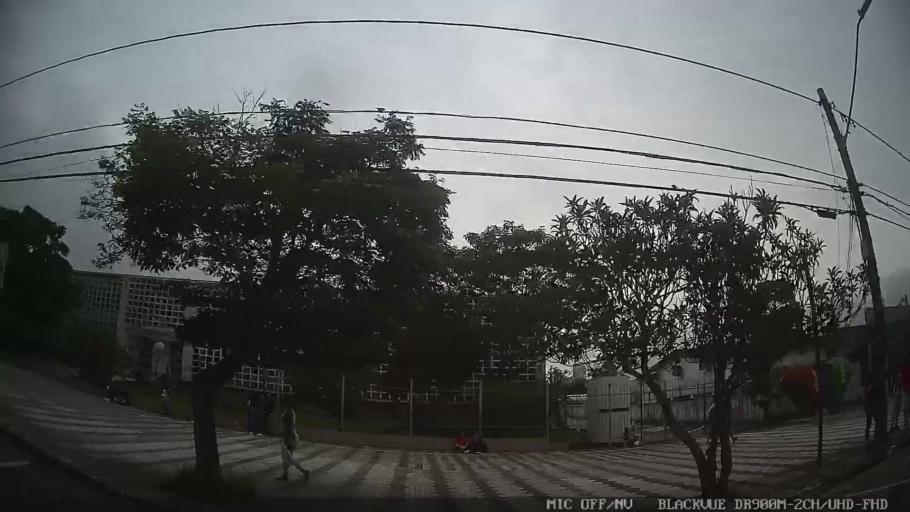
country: BR
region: Sao Paulo
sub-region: Mogi das Cruzes
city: Mogi das Cruzes
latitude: -23.5178
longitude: -46.1837
